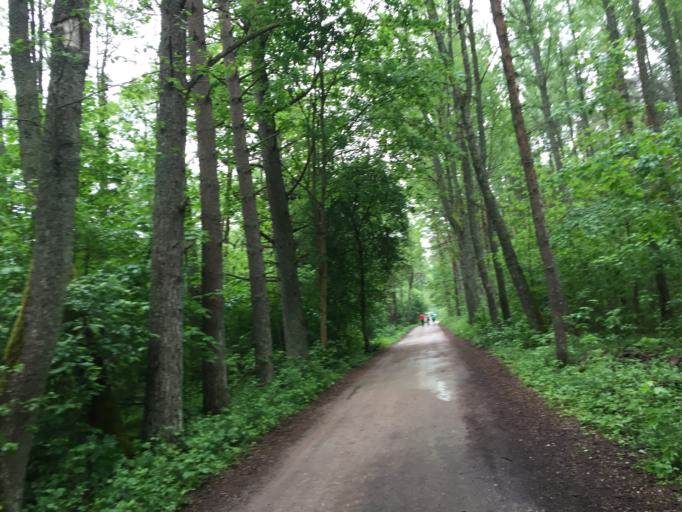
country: LT
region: Klaipedos apskritis
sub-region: Klaipeda
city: Klaipeda
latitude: 55.7973
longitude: 21.0717
